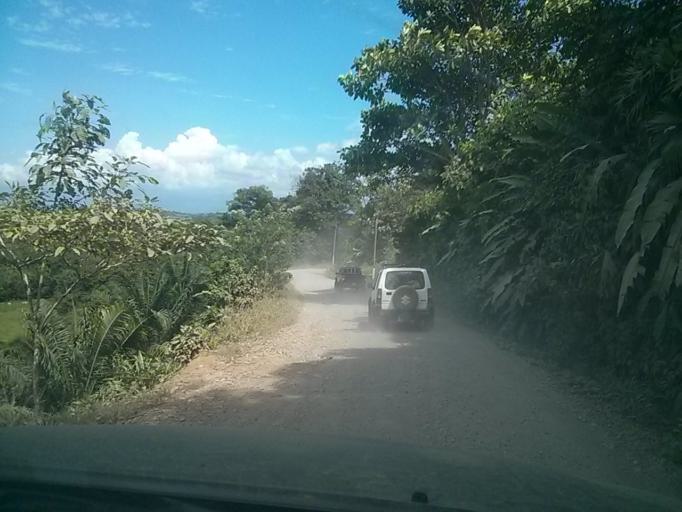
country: CR
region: Puntarenas
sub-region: Canton de Golfito
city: Golfito
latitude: 8.4545
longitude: -83.0517
